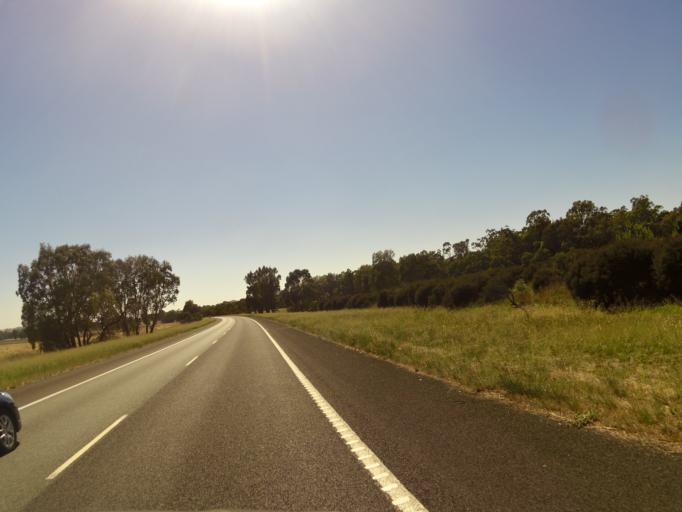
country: AU
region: Victoria
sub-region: Greater Shepparton
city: Shepparton
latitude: -36.8151
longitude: 145.4471
